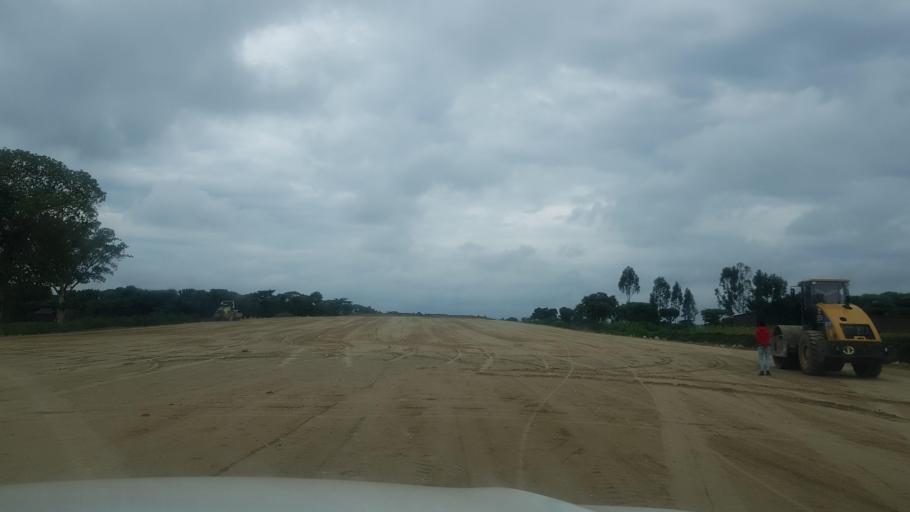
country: ET
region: Oromiya
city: Shashemene
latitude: 7.3240
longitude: 38.6323
